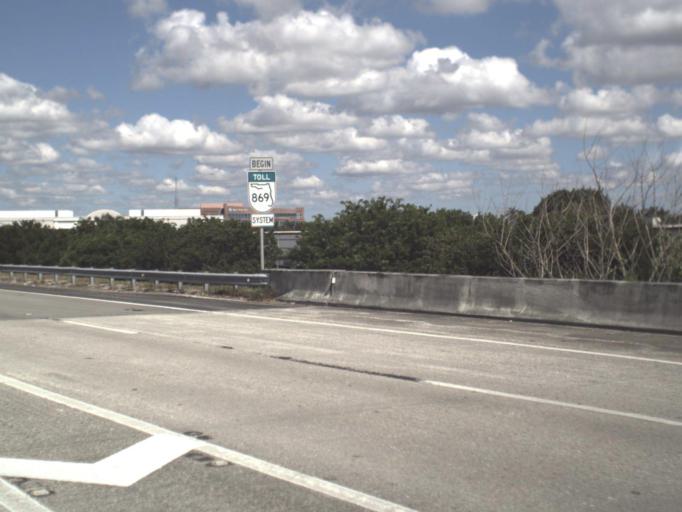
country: US
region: Florida
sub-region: Broward County
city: Weston
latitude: 26.1314
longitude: -80.3434
